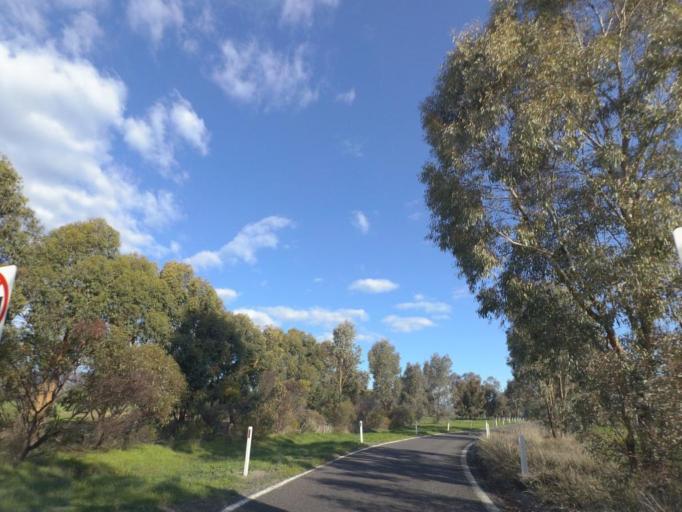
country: AU
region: Victoria
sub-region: Benalla
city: Benalla
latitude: -36.6952
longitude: 145.6596
